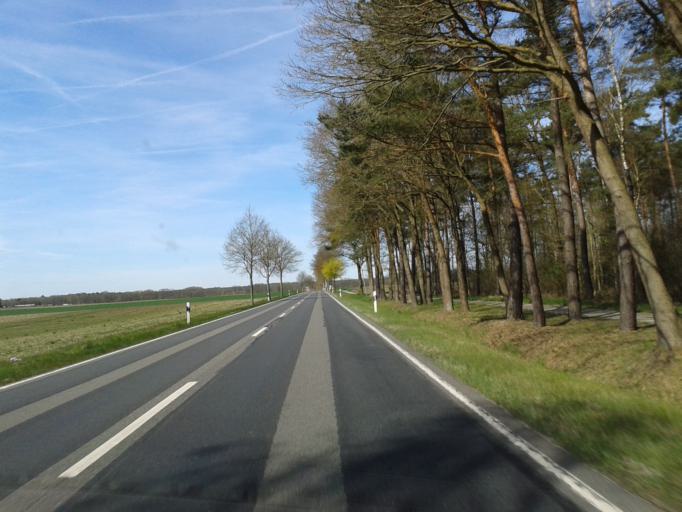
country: DE
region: Lower Saxony
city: Eimke
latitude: 52.9665
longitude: 10.3435
